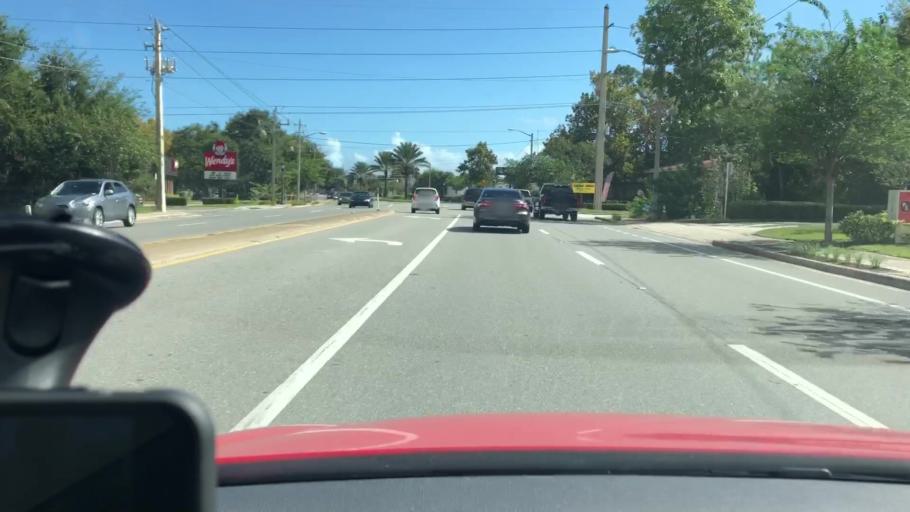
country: US
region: Florida
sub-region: Volusia County
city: Ormond Beach
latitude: 29.2812
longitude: -81.0668
